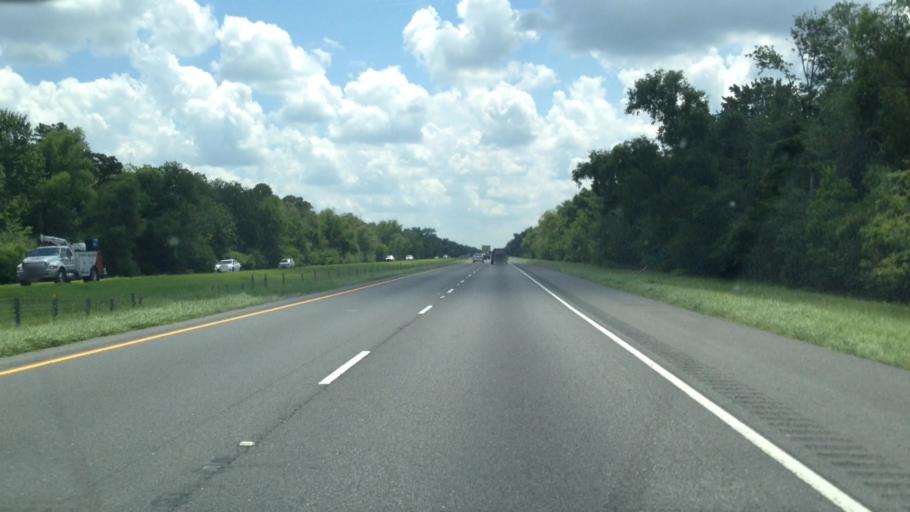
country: US
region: Louisiana
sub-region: Saint James Parish
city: Grand Point
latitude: 30.1392
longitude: -90.7450
